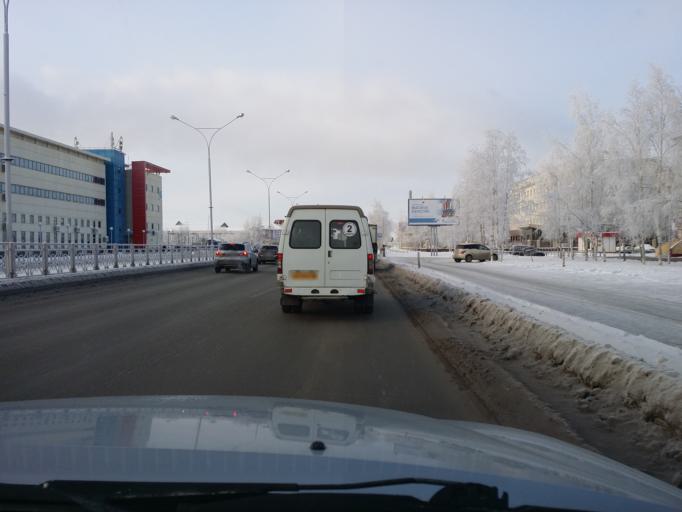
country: RU
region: Khanty-Mansiyskiy Avtonomnyy Okrug
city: Nizhnevartovsk
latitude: 60.9395
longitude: 76.5525
